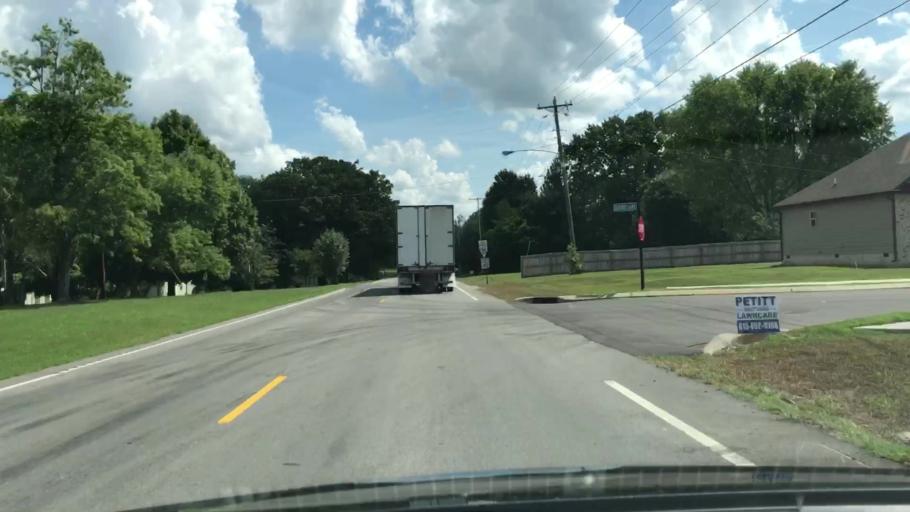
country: US
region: Tennessee
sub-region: Robertson County
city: Cross Plains
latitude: 36.5370
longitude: -86.6590
